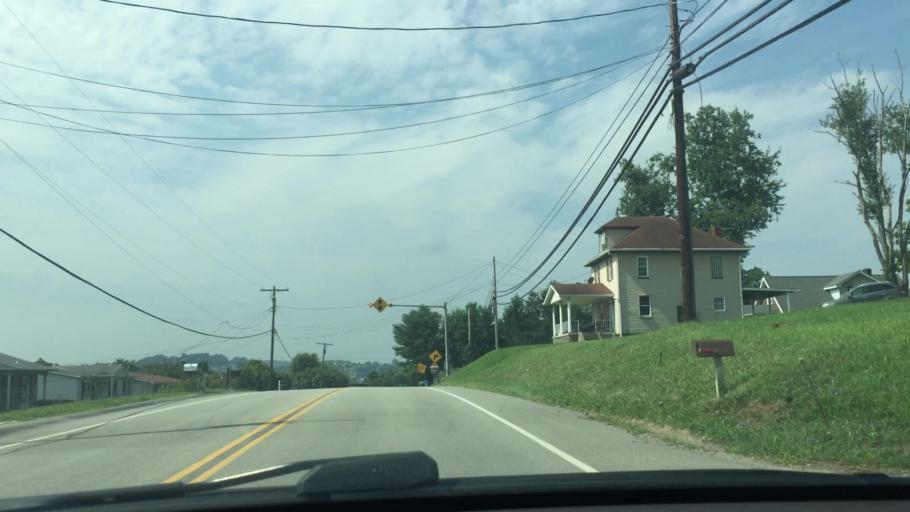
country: US
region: Pennsylvania
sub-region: Westmoreland County
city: Lynnwood-Pricedale
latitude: 40.1444
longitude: -79.8396
